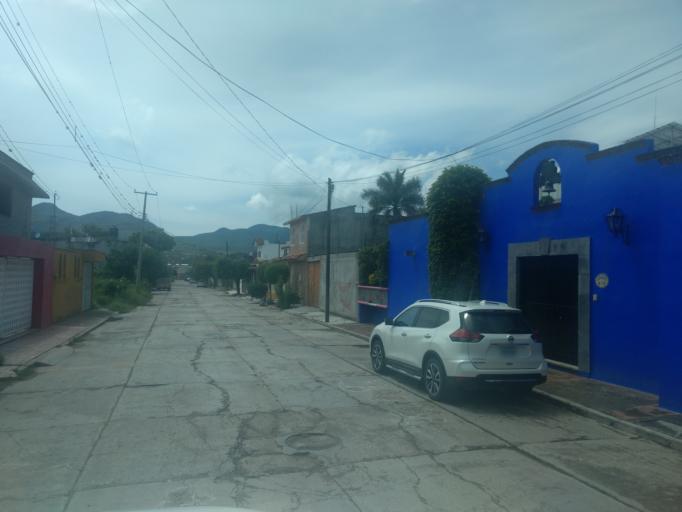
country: MX
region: Oaxaca
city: Ciudad de Huajuapam de Leon
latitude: 17.8004
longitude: -97.7795
